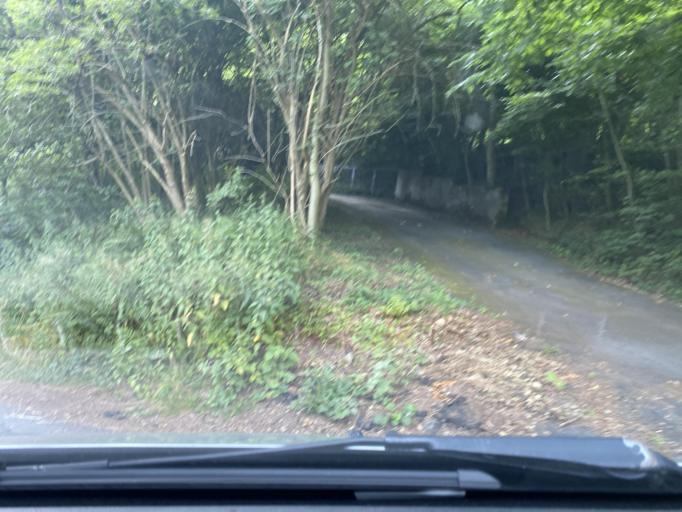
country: DE
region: North Rhine-Westphalia
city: Werdohl
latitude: 51.2691
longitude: 7.7704
